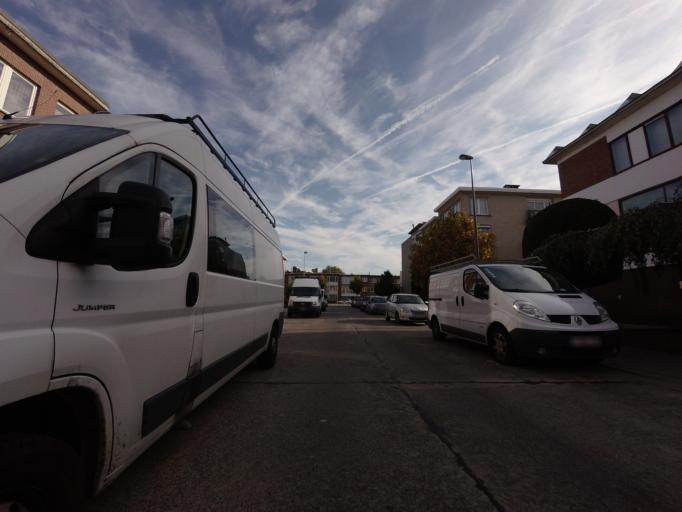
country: BE
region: Flanders
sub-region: Provincie Antwerpen
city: Borsbeek
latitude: 51.2295
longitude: 4.4756
